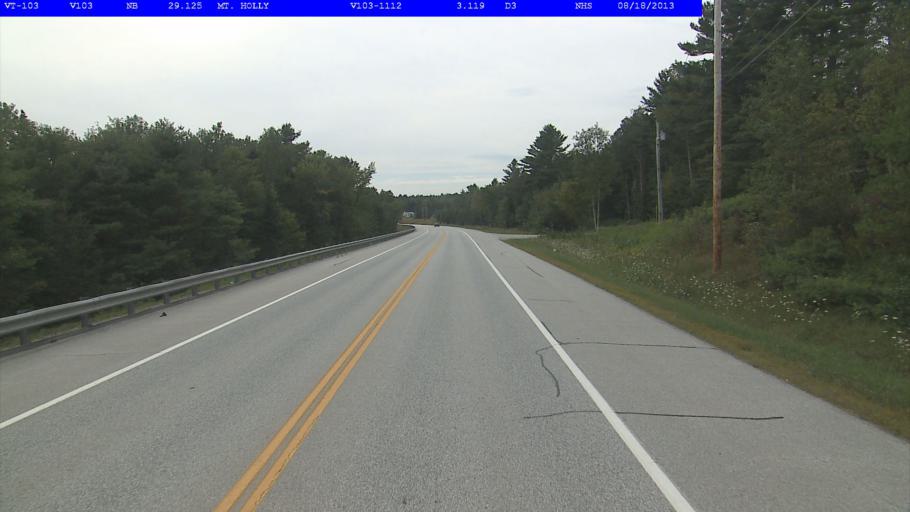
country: US
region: Vermont
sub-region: Rutland County
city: Rutland
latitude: 43.4527
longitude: -72.7875
